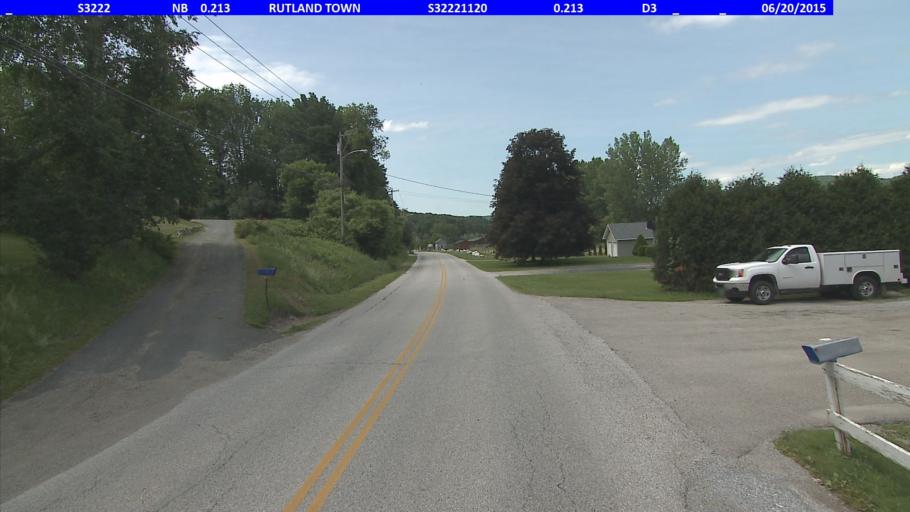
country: US
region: Vermont
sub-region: Rutland County
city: West Rutland
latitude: 43.6023
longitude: -73.0219
